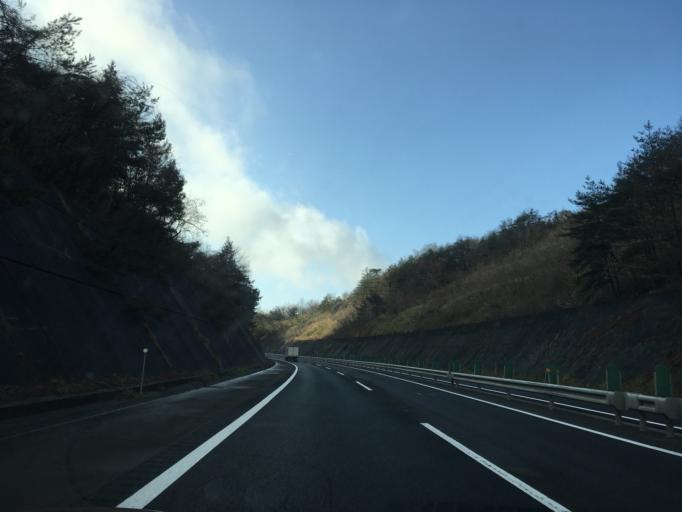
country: JP
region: Miyagi
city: Okawara
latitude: 38.1522
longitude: 140.6974
